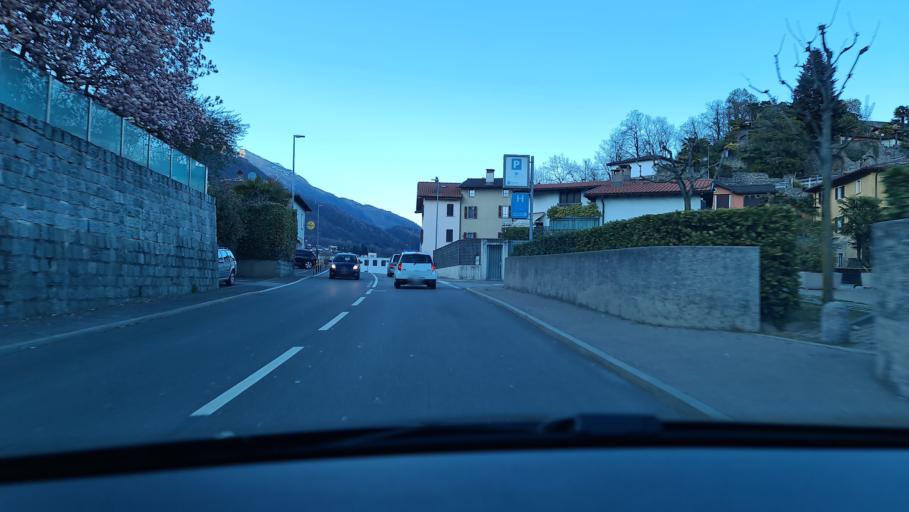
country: CH
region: Ticino
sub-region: Lugano District
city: Gravesano
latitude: 46.0396
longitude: 8.9234
